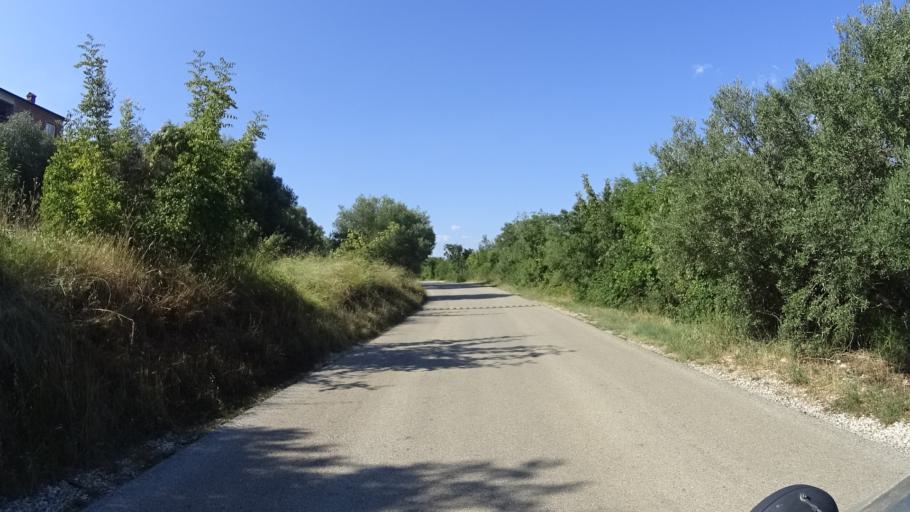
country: HR
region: Istarska
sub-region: Grad Labin
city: Rabac
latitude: 45.0029
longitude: 14.1628
